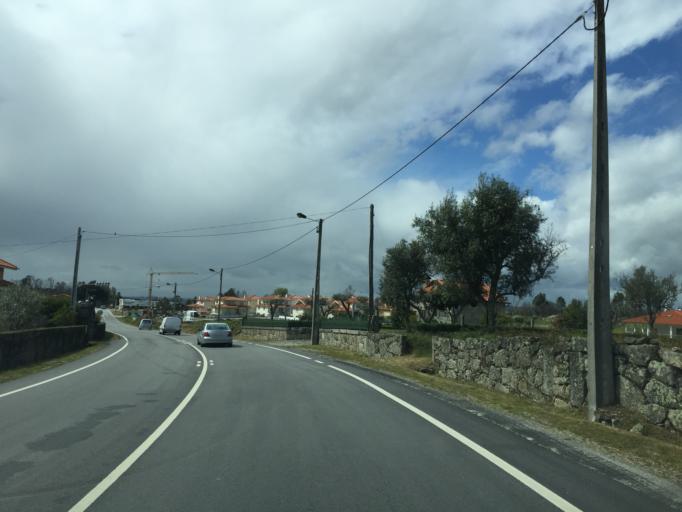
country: PT
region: Guarda
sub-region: Seia
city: Seia
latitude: 40.5072
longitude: -7.6180
